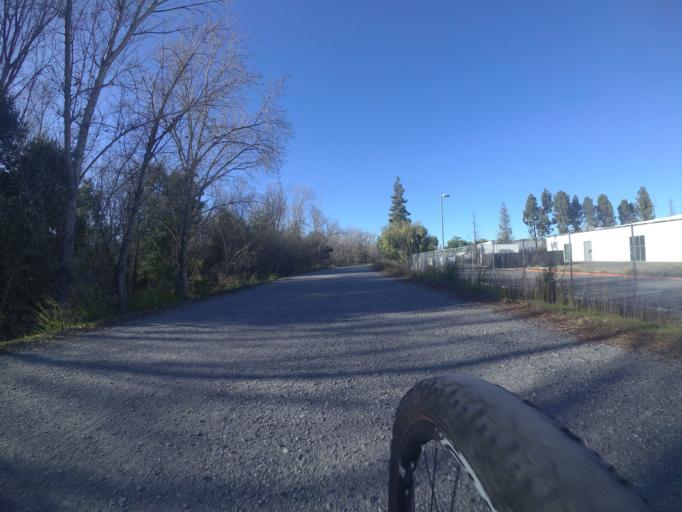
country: US
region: California
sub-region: Santa Clara County
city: Milpitas
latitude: 37.4010
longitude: -121.9160
